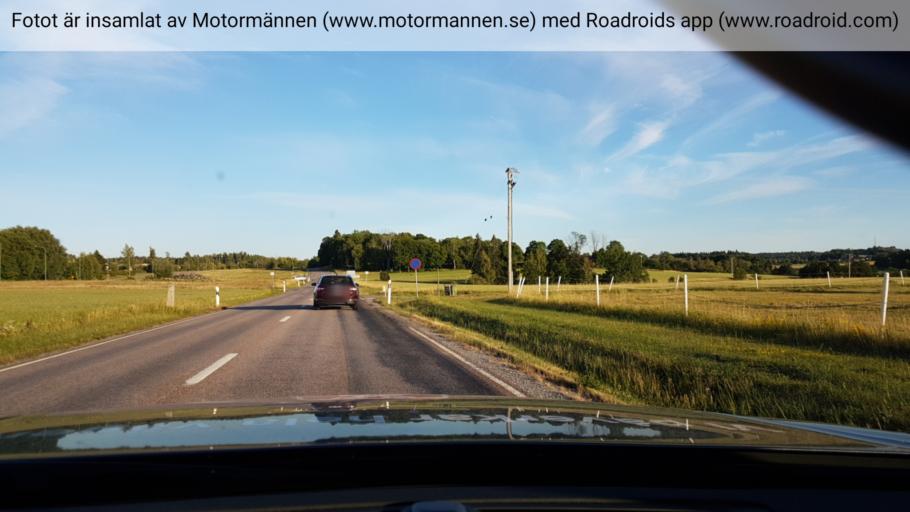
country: SE
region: Vaestmanland
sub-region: Vasteras
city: Vasteras
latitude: 59.6494
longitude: 16.4973
